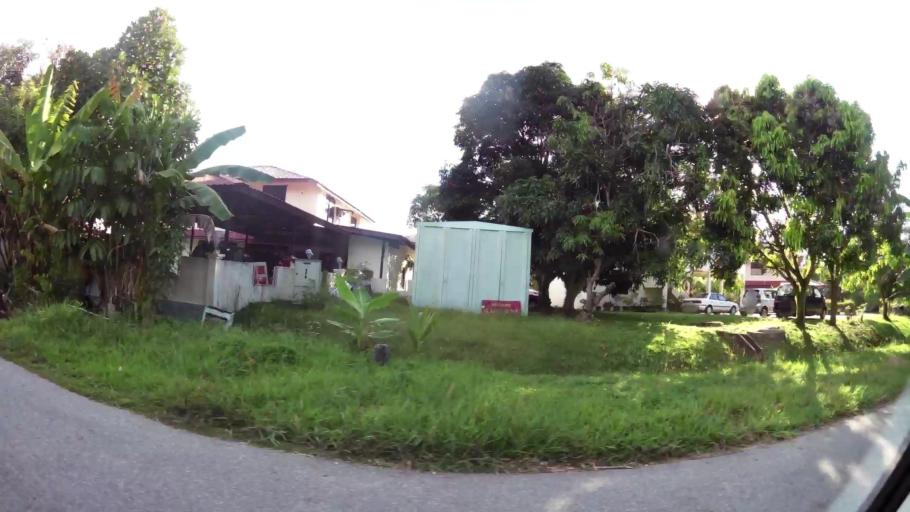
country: BN
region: Brunei and Muara
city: Bandar Seri Begawan
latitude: 4.9851
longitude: 114.9683
